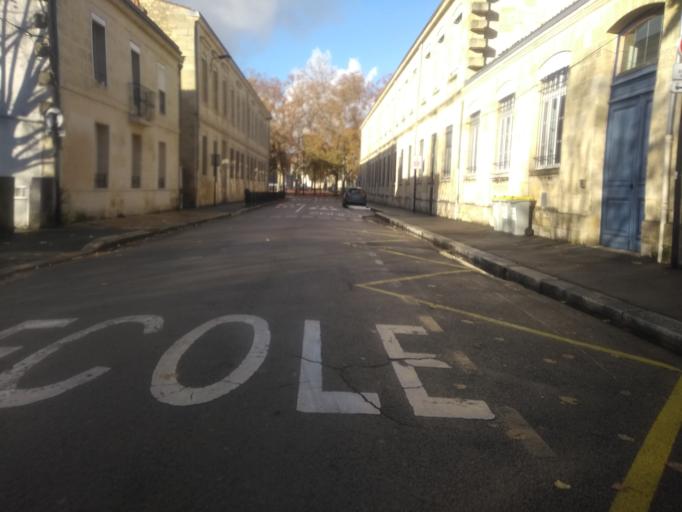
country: FR
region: Aquitaine
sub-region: Departement de la Gironde
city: Begles
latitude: 44.8231
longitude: -0.5509
